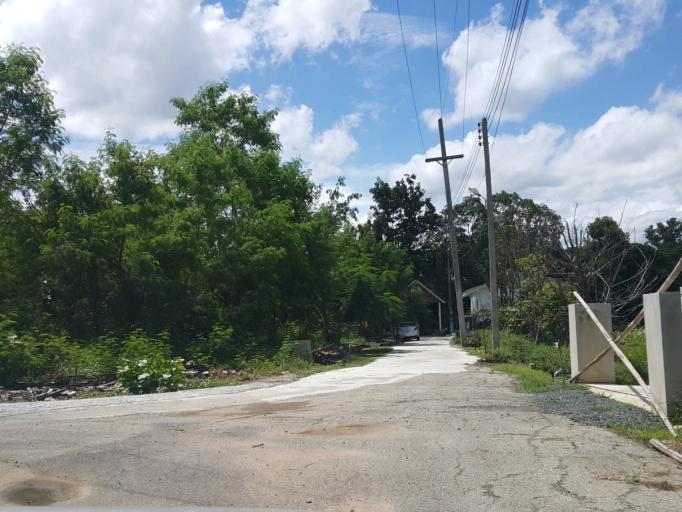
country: TH
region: Chiang Mai
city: San Kamphaeng
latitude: 18.7677
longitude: 99.1204
